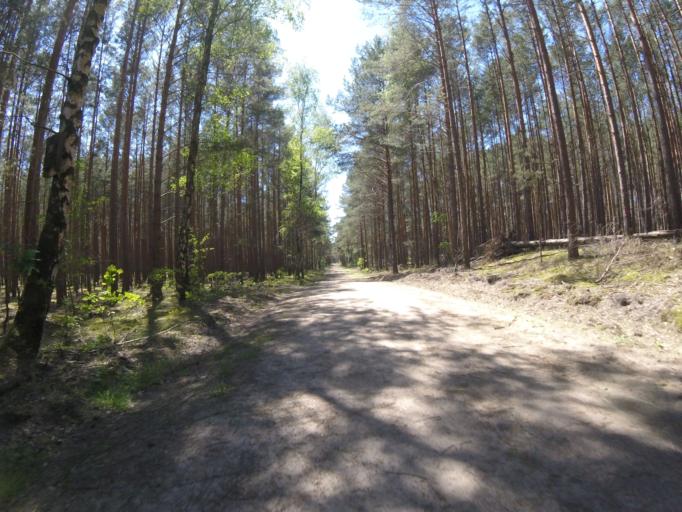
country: DE
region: Brandenburg
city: Teupitz
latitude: 52.1136
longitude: 13.6058
